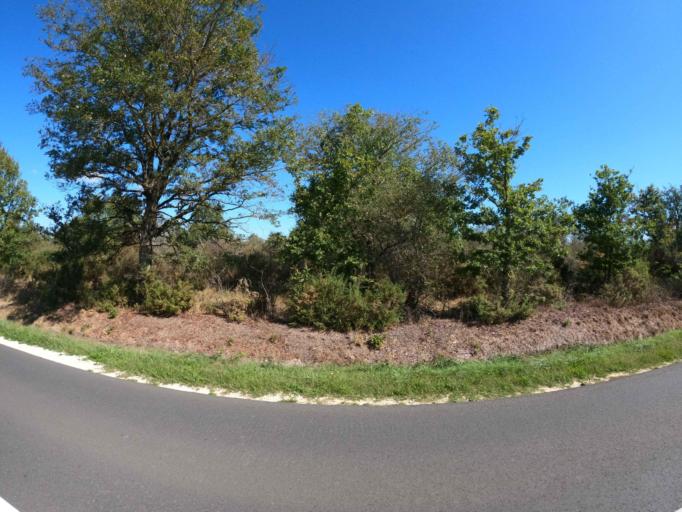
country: FR
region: Poitou-Charentes
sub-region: Departement de la Vienne
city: Lathus-Saint-Remy
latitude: 46.3720
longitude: 0.9319
